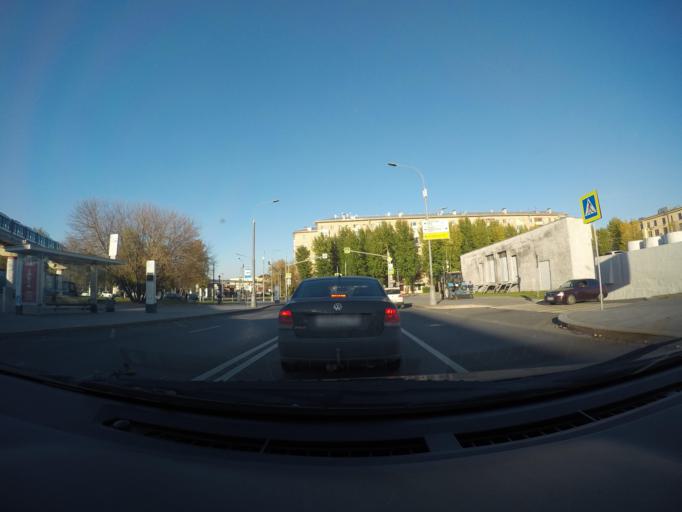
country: RU
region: Moscow
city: Leonovo
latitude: 55.8296
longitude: 37.6458
